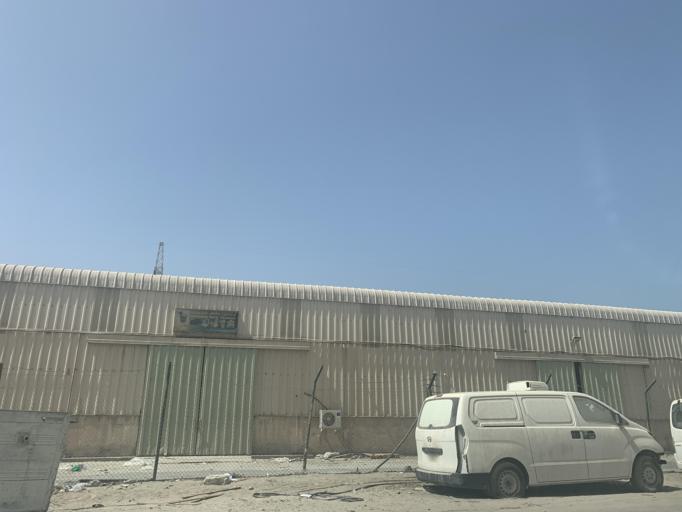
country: BH
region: Northern
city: Sitrah
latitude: 26.1761
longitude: 50.6123
